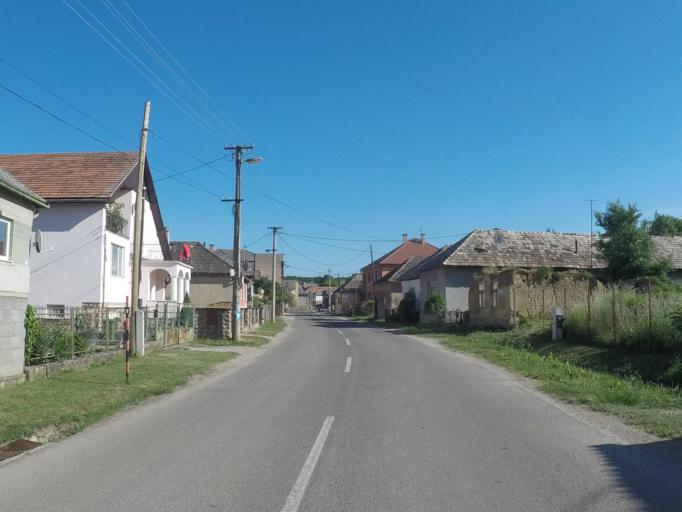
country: SK
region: Kosicky
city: Roznava
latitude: 48.4954
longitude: 20.4373
